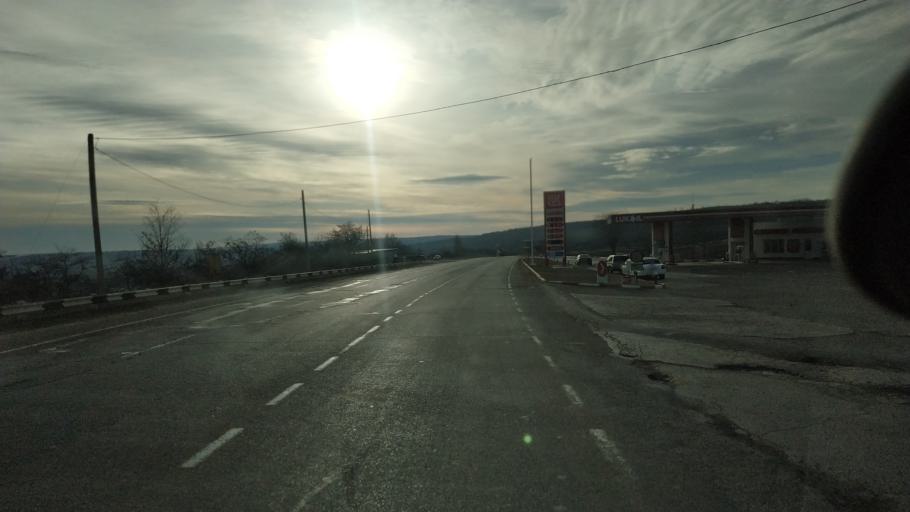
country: MD
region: Chisinau
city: Vadul lui Voda
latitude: 47.0885
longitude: 29.0707
